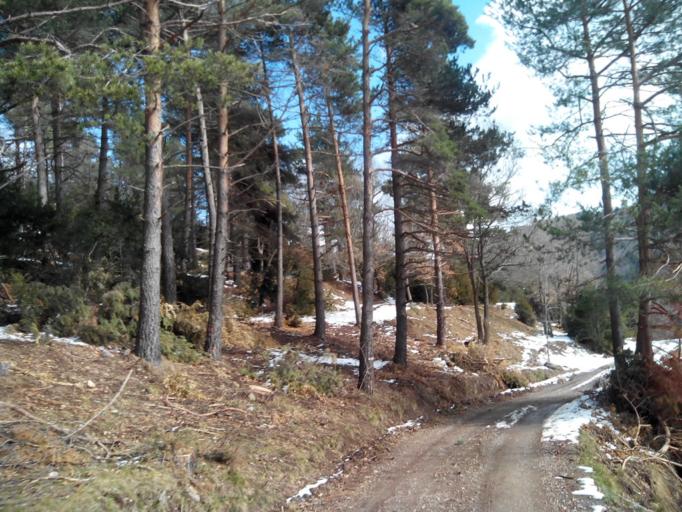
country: ES
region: Catalonia
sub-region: Provincia de Barcelona
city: Vilada
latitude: 42.1857
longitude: 1.9316
